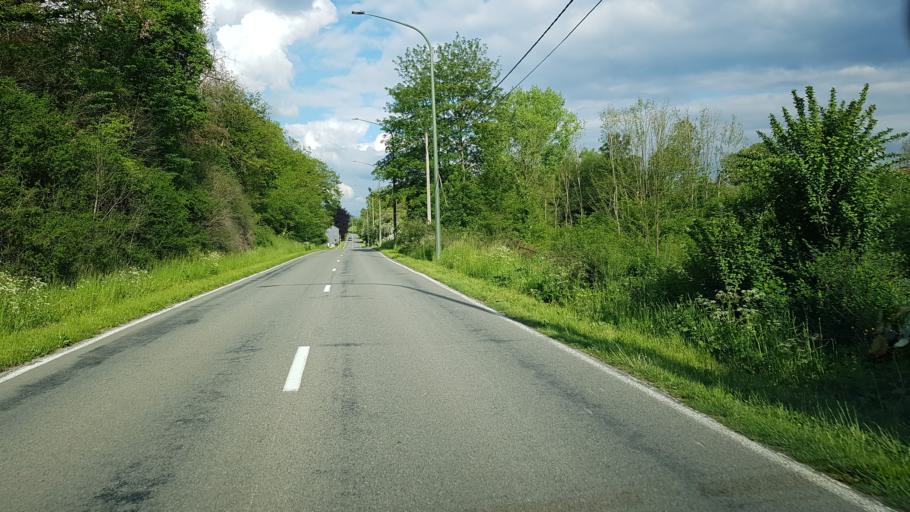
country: BE
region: Wallonia
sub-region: Province de Liege
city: Trooz
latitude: 50.5360
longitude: 5.6999
